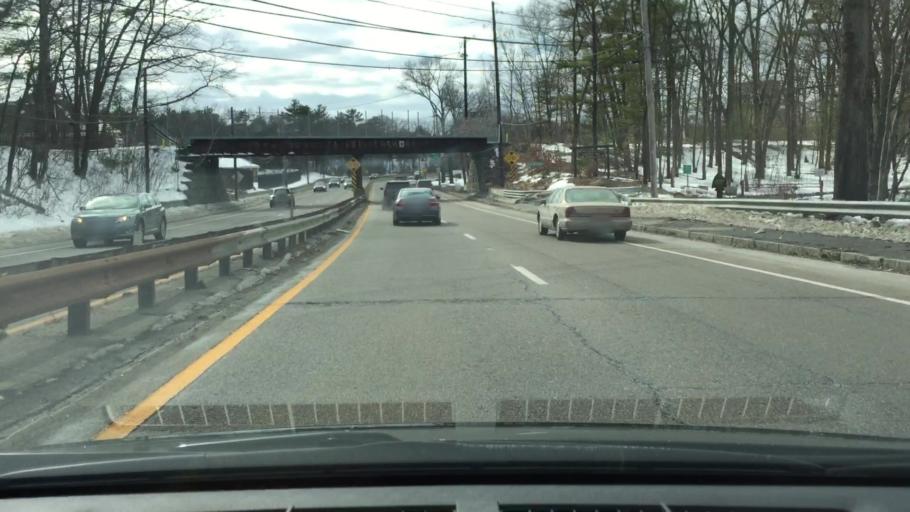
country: US
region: Massachusetts
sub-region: Middlesex County
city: Cochituate
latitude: 42.2991
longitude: -71.3673
